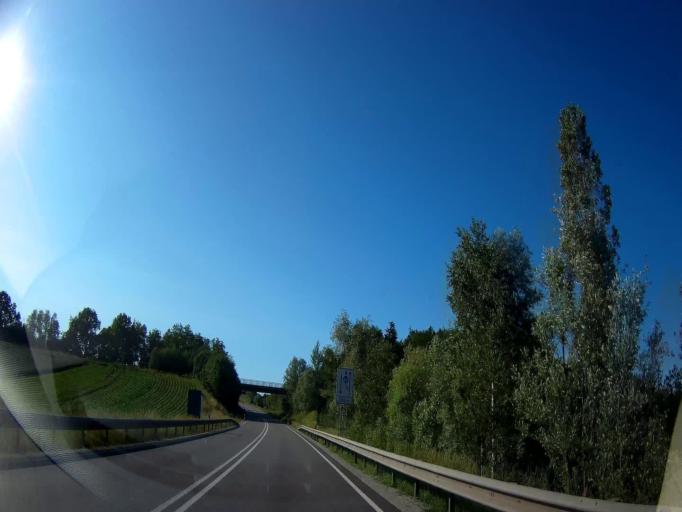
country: DE
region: Bavaria
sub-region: Lower Bavaria
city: Malgersdorf
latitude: 48.5342
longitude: 12.7523
